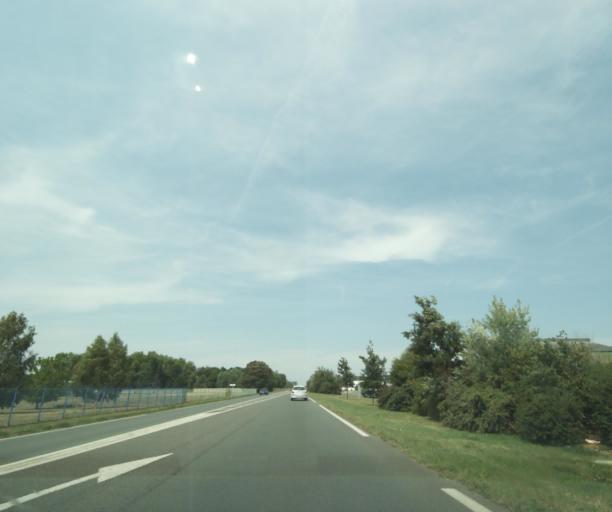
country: FR
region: Poitou-Charentes
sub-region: Departement de la Vienne
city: Antran
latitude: 46.8495
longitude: 0.5509
